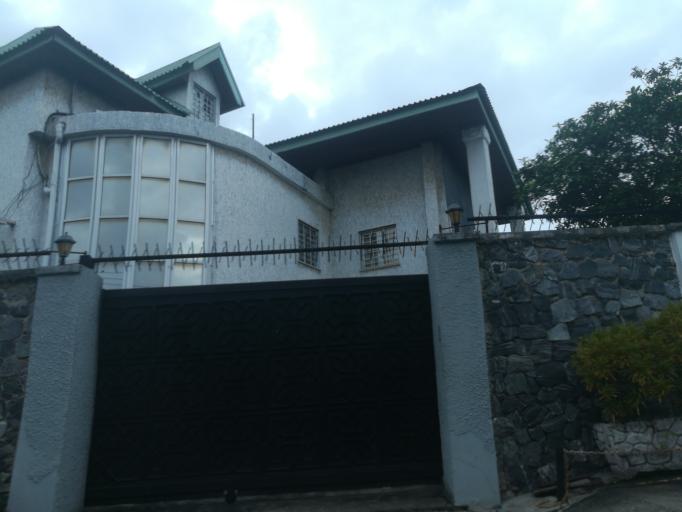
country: NG
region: Lagos
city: Ikoyi
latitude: 6.4409
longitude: 3.4180
